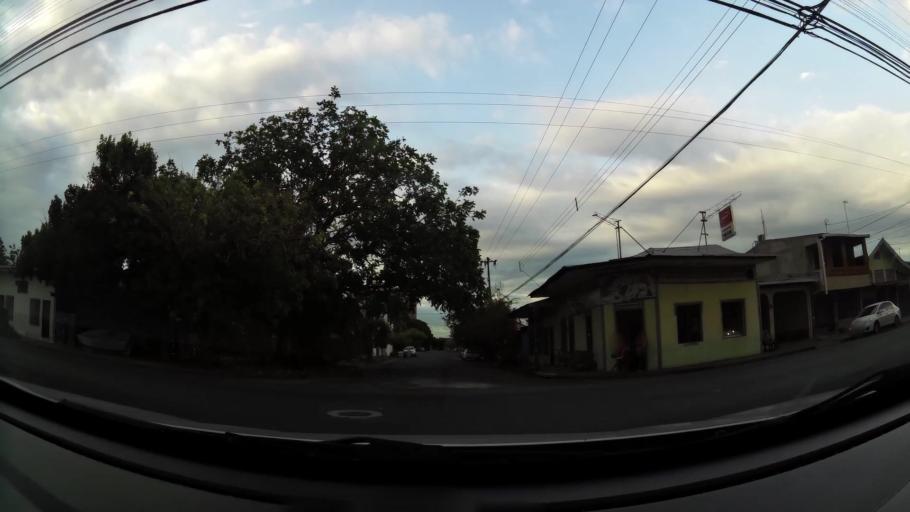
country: CR
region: Puntarenas
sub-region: Canton Central de Puntarenas
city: Puntarenas
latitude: 9.9770
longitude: -84.8380
